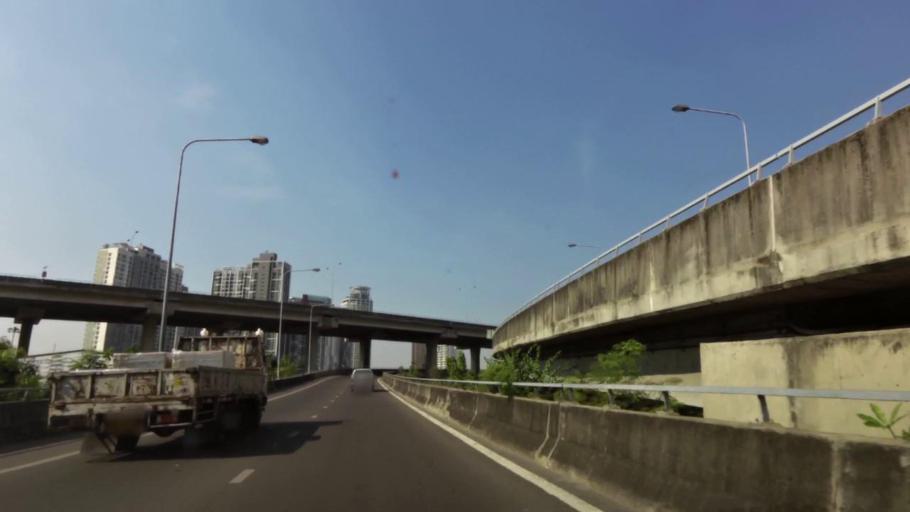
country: TH
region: Bangkok
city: Phra Khanong
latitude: 13.7082
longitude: 100.5967
